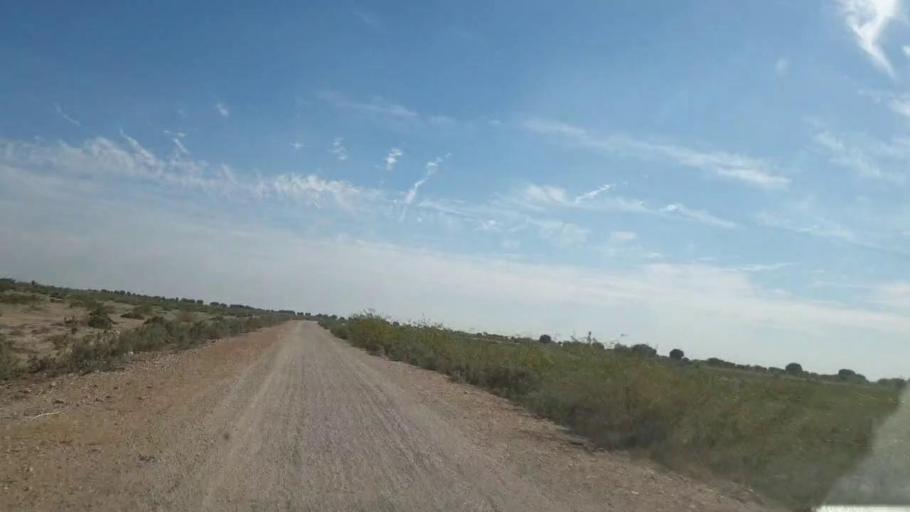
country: PK
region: Sindh
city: Pithoro
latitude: 25.5606
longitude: 69.3026
